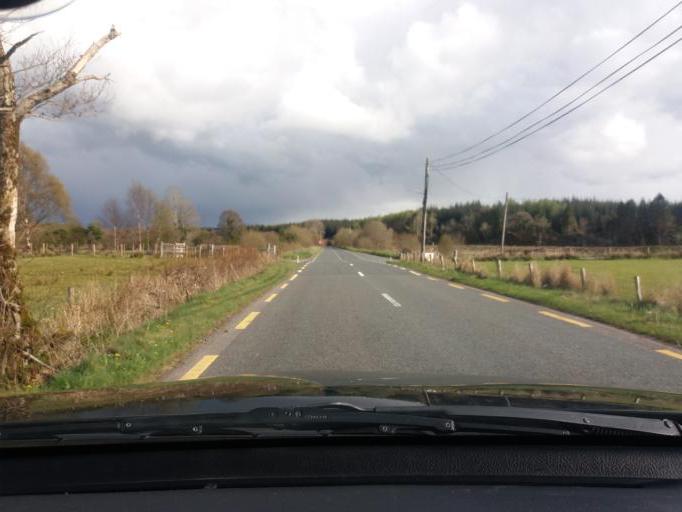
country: IE
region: Connaught
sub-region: County Leitrim
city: Manorhamilton
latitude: 54.3347
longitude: -8.2186
